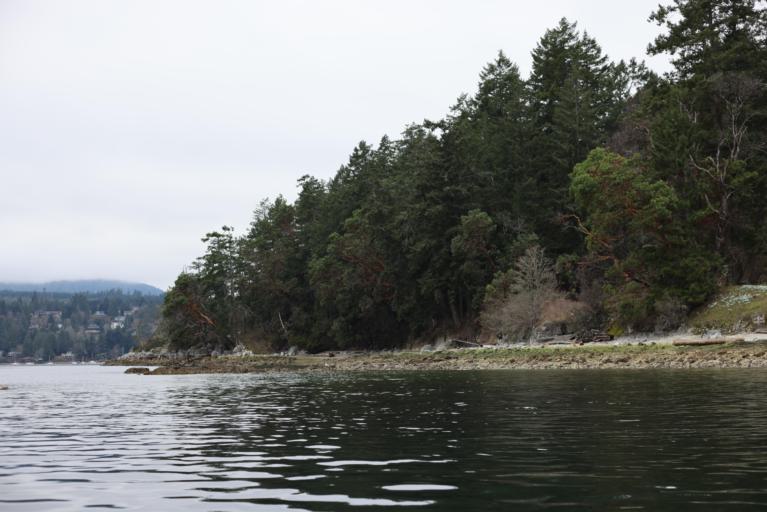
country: CA
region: British Columbia
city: North Saanich
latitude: 48.6561
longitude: -123.5372
